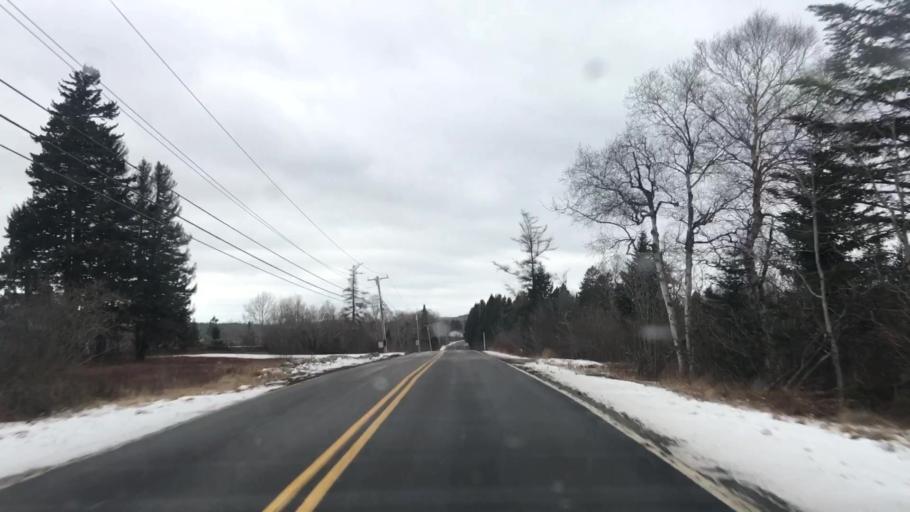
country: US
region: Maine
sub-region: Washington County
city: Machiasport
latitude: 44.7029
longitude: -67.3361
